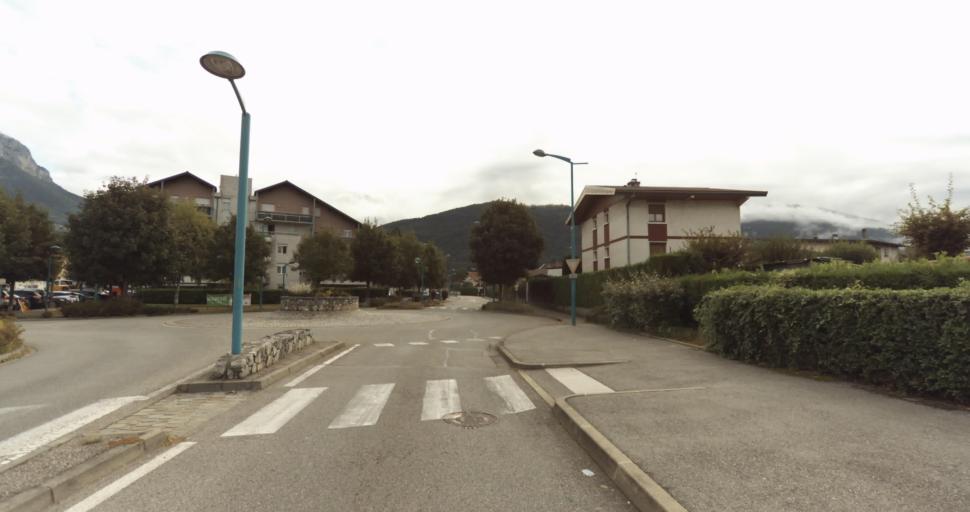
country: FR
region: Rhone-Alpes
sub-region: Departement de la Savoie
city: La Ravoire
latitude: 45.5714
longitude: 5.9658
